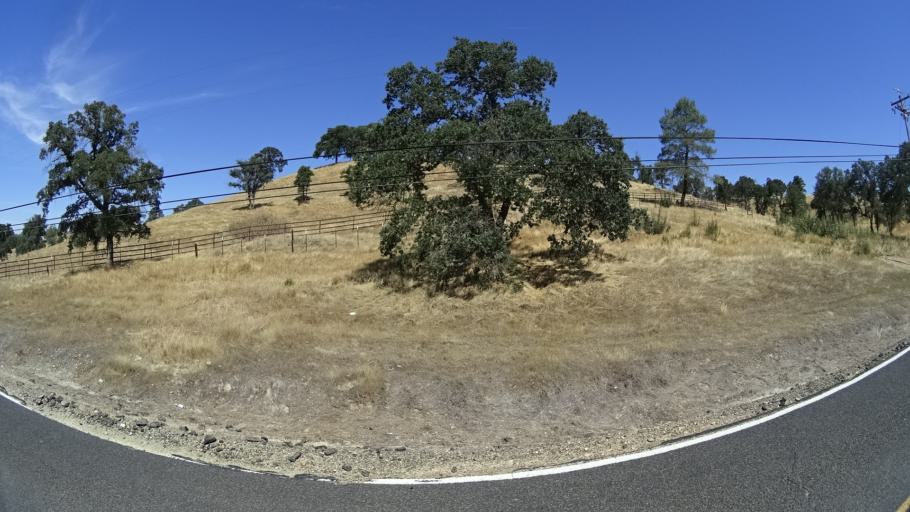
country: US
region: California
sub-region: Calaveras County
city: Rancho Calaveras
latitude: 38.1659
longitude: -120.8909
